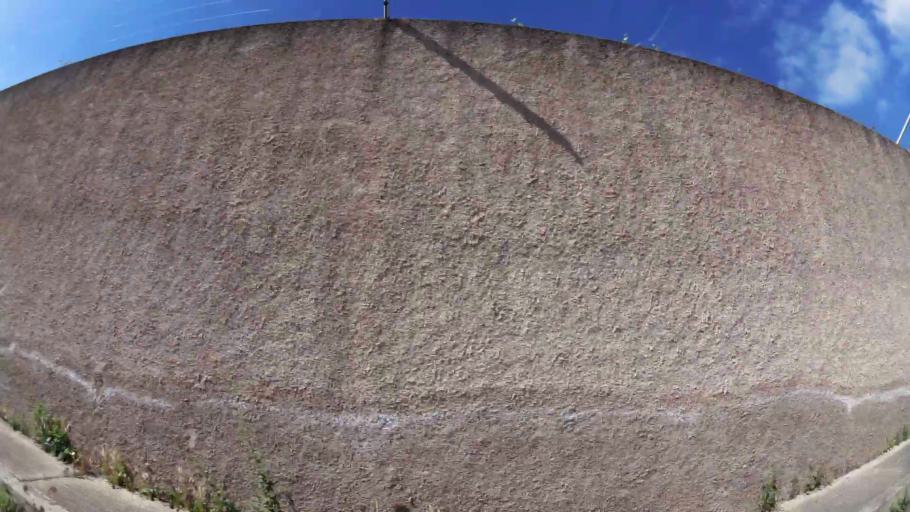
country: MA
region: Fes-Boulemane
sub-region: Fes
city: Fes
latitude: 34.0299
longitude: -5.0173
